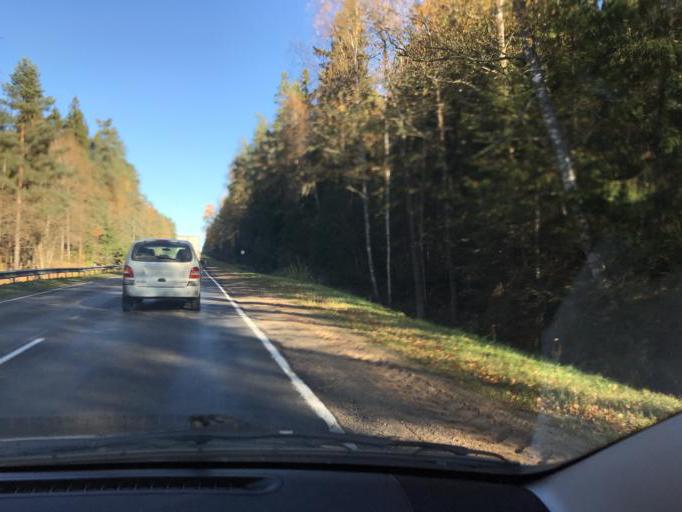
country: BY
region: Vitebsk
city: Polatsk
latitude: 55.3390
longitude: 28.7925
